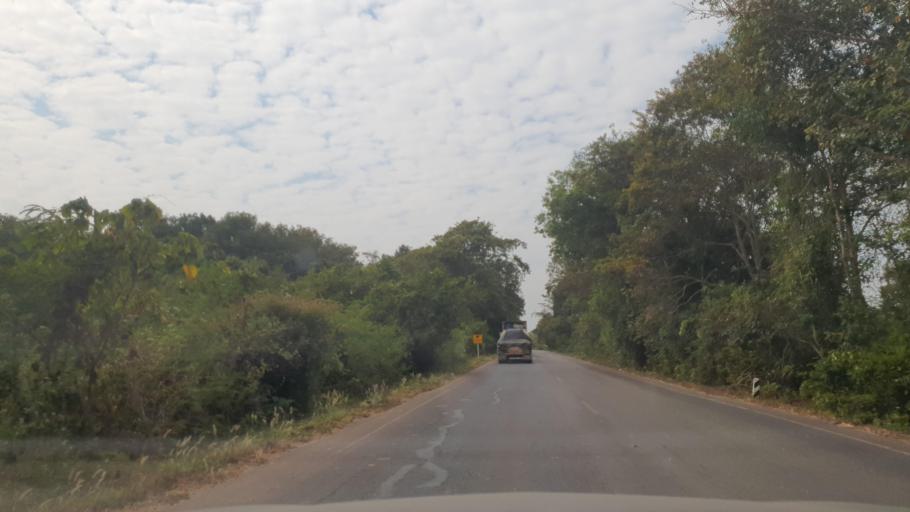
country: TH
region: Changwat Bueng Kan
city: Bung Khla
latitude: 18.3037
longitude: 103.9606
